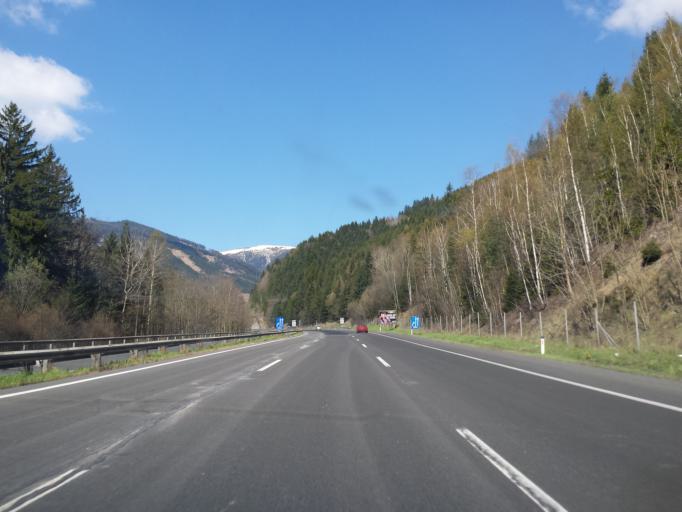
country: AT
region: Styria
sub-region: Politischer Bezirk Graz-Umgebung
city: Ubelbach
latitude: 47.2455
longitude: 15.1789
